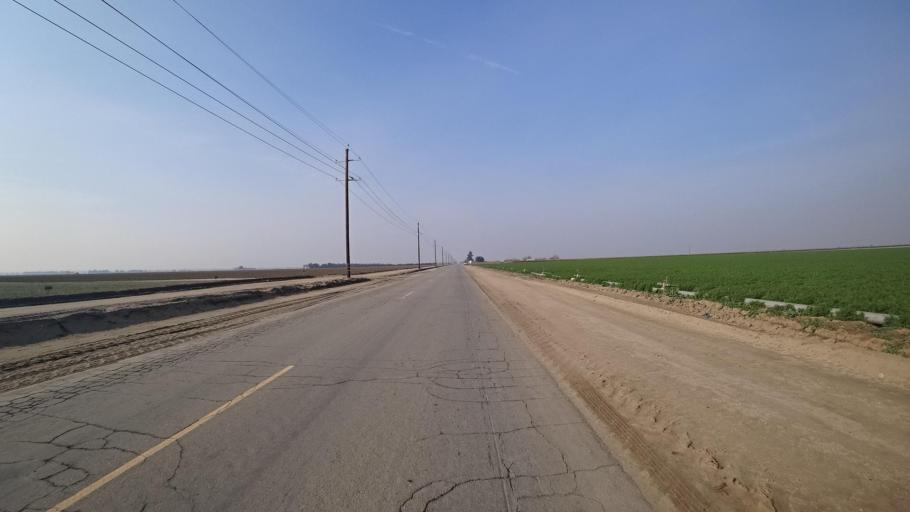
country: US
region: California
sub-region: Kern County
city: Arvin
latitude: 35.0928
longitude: -118.8549
